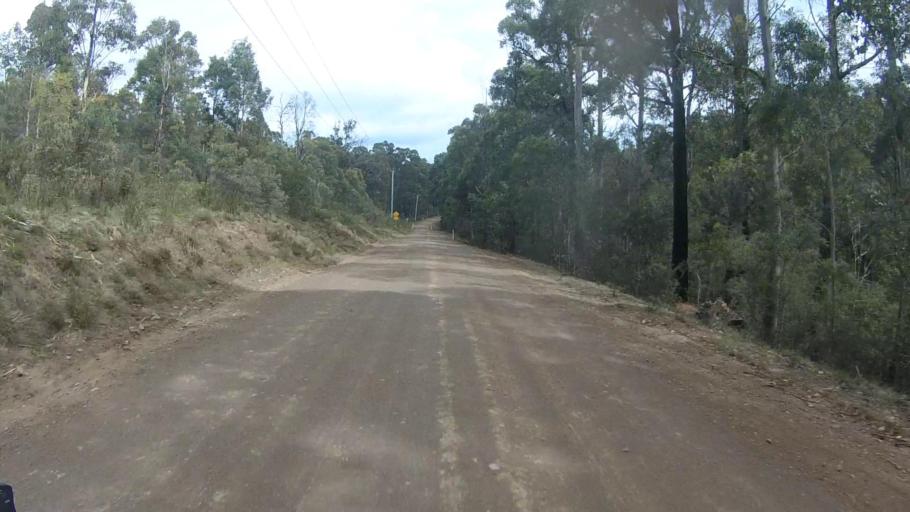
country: AU
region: Tasmania
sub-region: Sorell
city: Sorell
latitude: -42.7521
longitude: 147.7959
